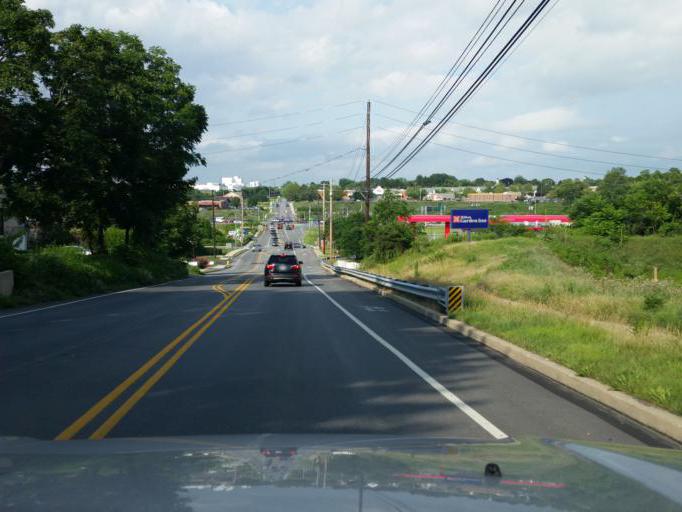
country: US
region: Pennsylvania
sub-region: Dauphin County
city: Hummelstown
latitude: 40.2678
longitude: -76.6929
